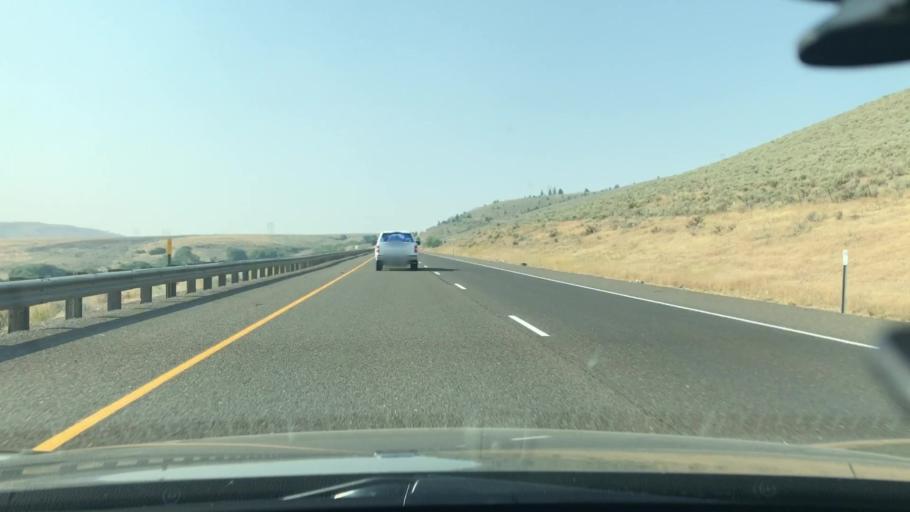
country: US
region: Oregon
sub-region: Union County
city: Union
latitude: 45.1399
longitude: -117.9682
